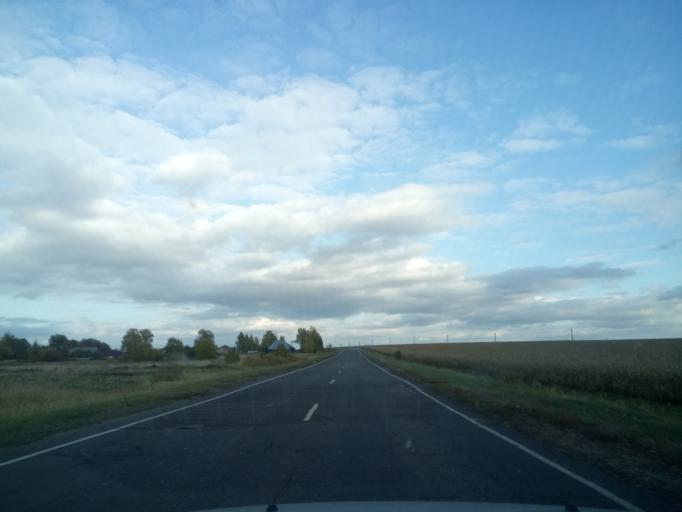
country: RU
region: Nizjnij Novgorod
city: Bol'shoye Boldino
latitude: 54.9906
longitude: 45.3119
